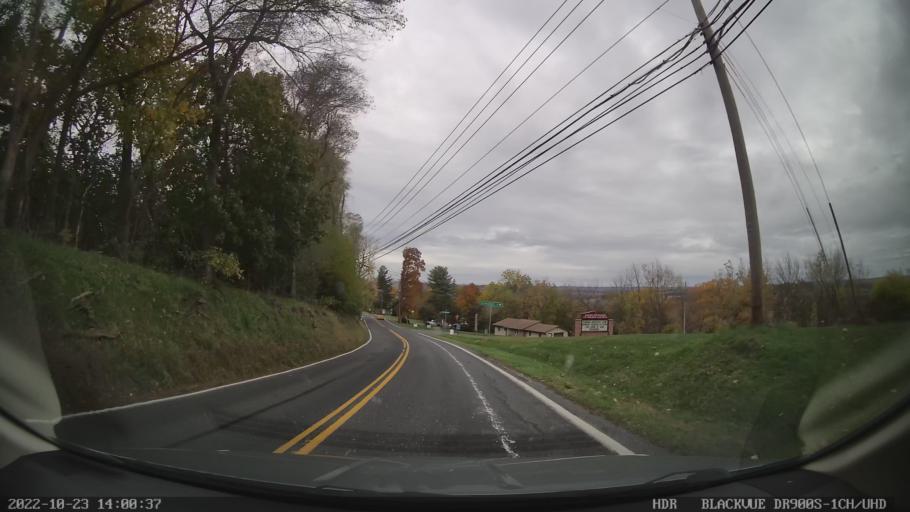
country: US
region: Pennsylvania
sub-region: Northampton County
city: Northampton
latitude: 40.7168
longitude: -75.4859
